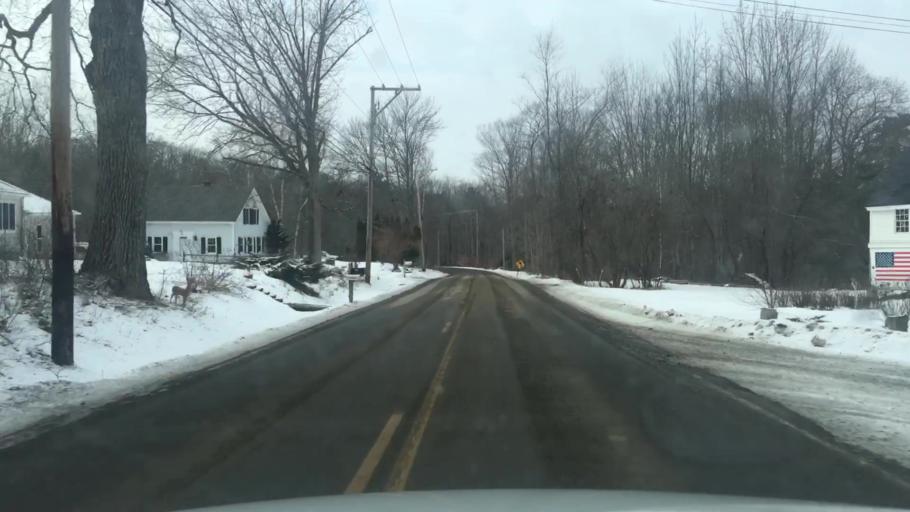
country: US
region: Maine
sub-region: Waldo County
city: Lincolnville
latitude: 44.2908
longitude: -69.0711
